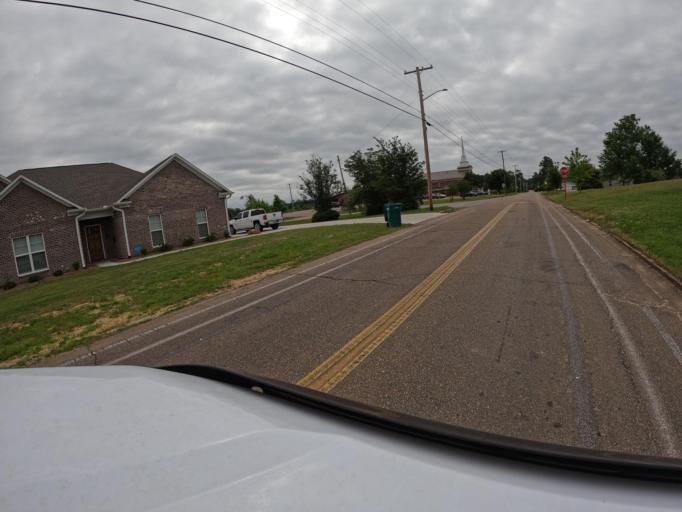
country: US
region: Mississippi
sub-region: Lee County
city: Tupelo
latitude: 34.2772
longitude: -88.7264
